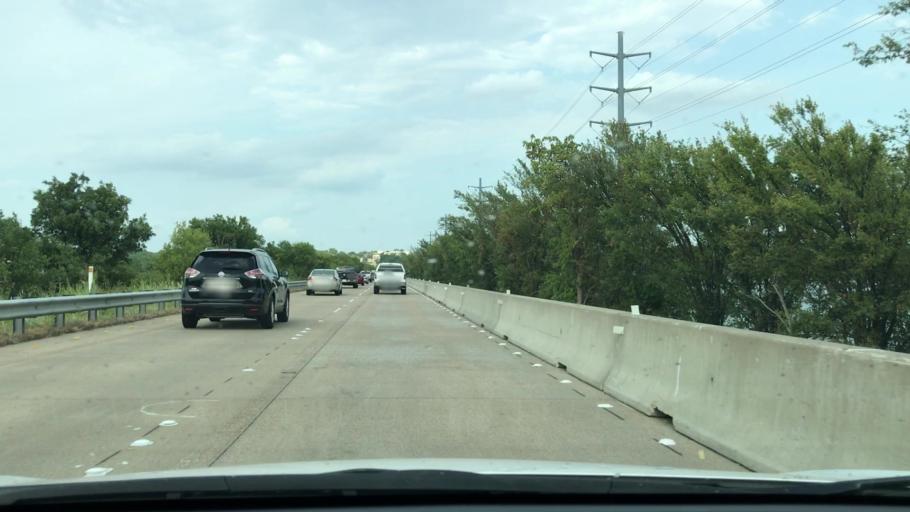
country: US
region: Texas
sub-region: Rockwall County
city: Rockwall
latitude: 32.9267
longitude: -96.4817
